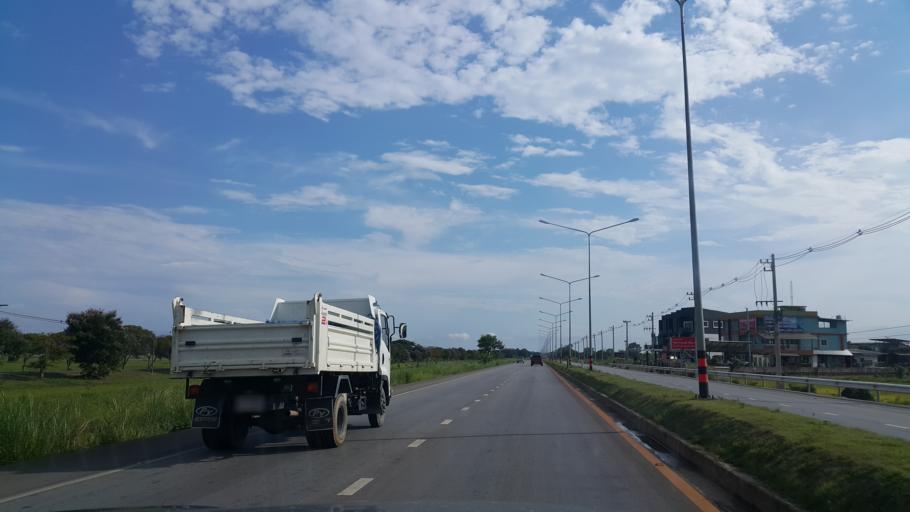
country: TH
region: Chiang Rai
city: Chiang Rai
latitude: 19.9439
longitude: 99.8708
